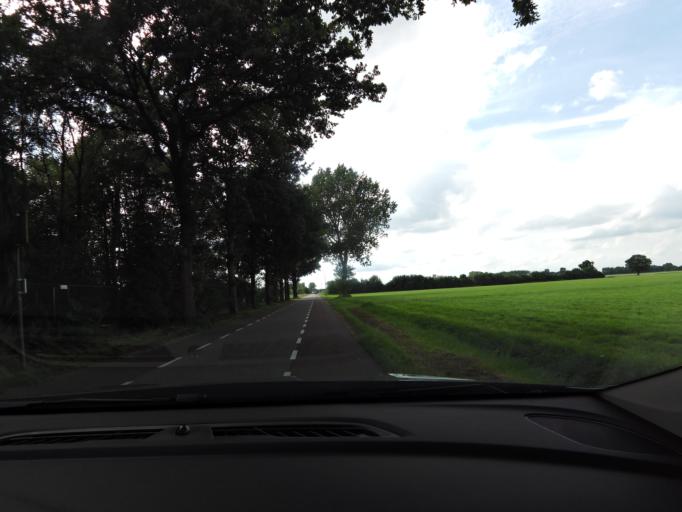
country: BE
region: Flanders
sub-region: Provincie Antwerpen
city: Hoogstraten
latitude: 51.4173
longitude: 4.7818
